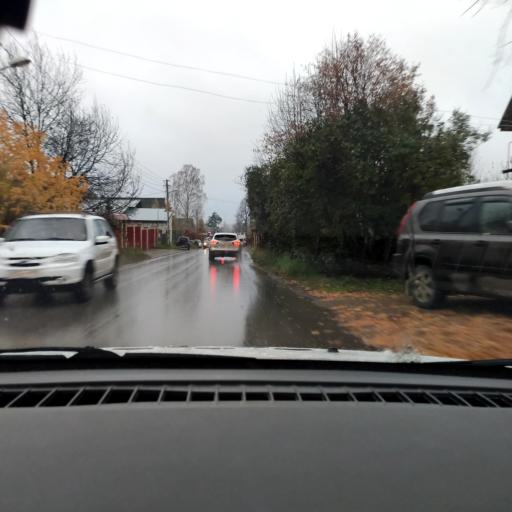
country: RU
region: Perm
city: Kondratovo
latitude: 58.0485
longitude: 56.1205
